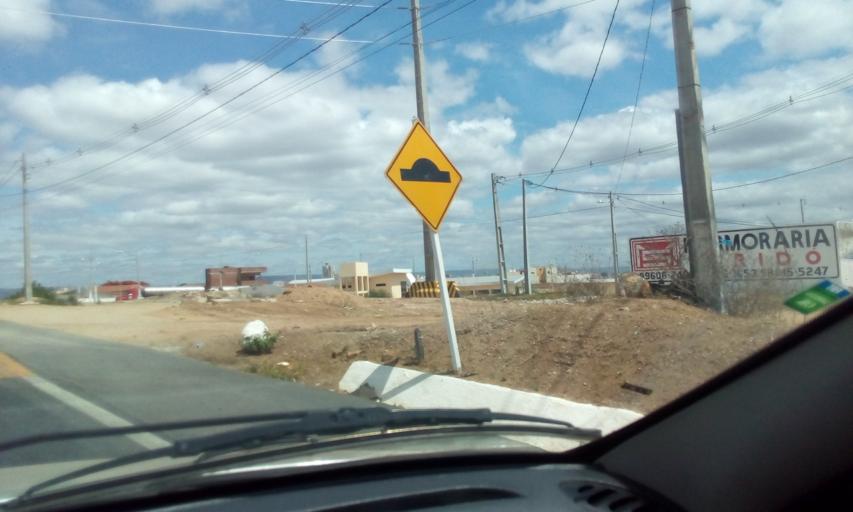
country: BR
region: Rio Grande do Norte
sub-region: Currais Novos
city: Currais Novos
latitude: -6.2753
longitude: -36.5232
